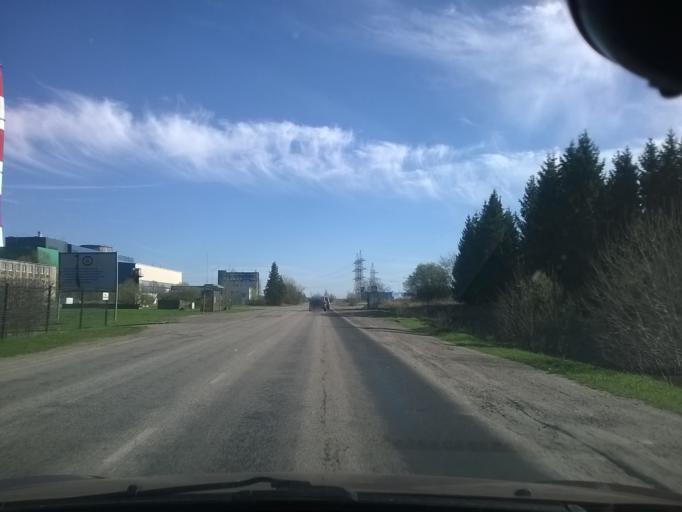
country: EE
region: Harju
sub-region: Joelaehtme vald
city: Loo
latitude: 59.4557
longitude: 24.9192
